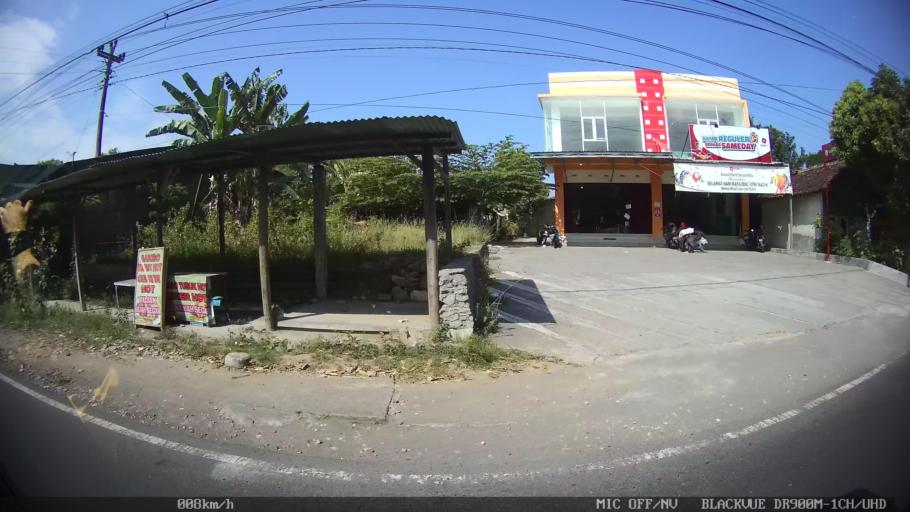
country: ID
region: Daerah Istimewa Yogyakarta
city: Sewon
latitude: -7.8732
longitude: 110.3918
